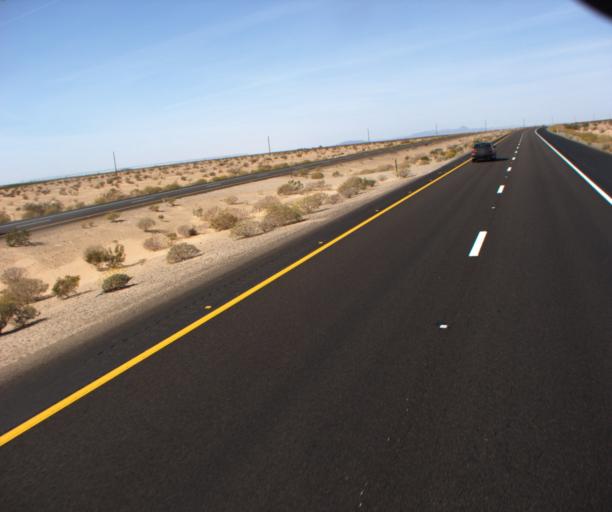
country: US
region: Arizona
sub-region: Yuma County
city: Somerton
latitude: 32.5098
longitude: -114.5590
